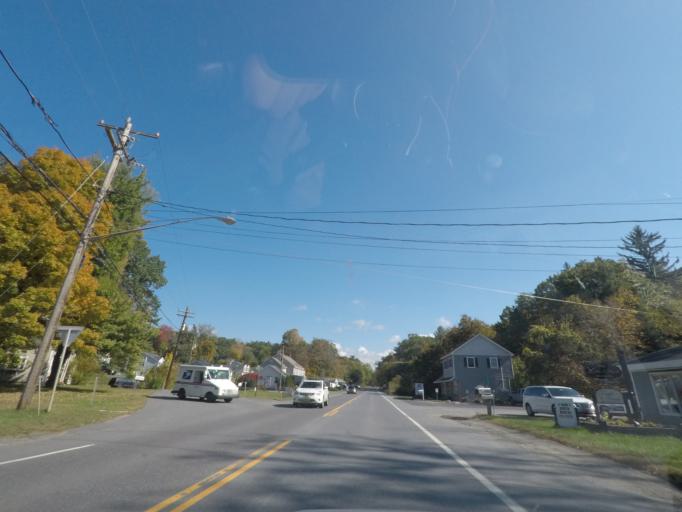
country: US
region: New York
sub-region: Rensselaer County
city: West Sand Lake
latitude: 42.6458
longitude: -73.5958
